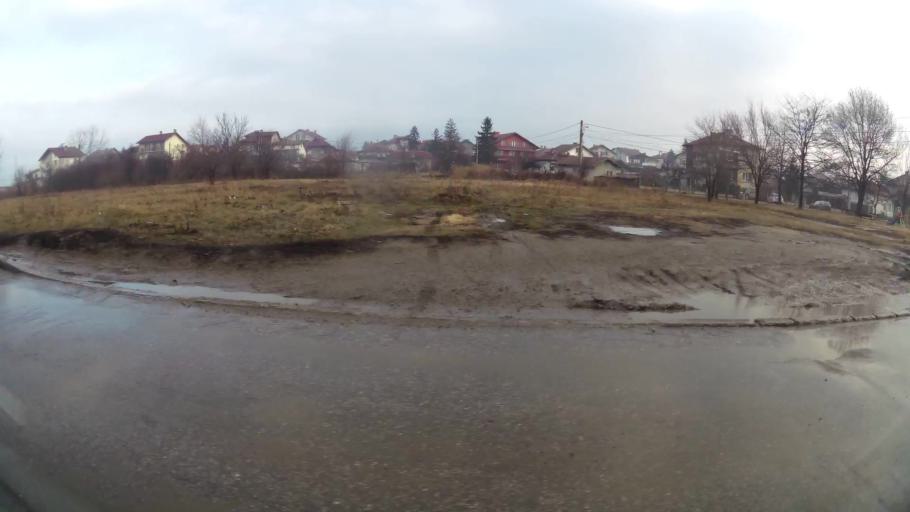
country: BG
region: Sofia-Capital
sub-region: Stolichna Obshtina
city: Sofia
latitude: 42.7373
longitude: 23.3379
